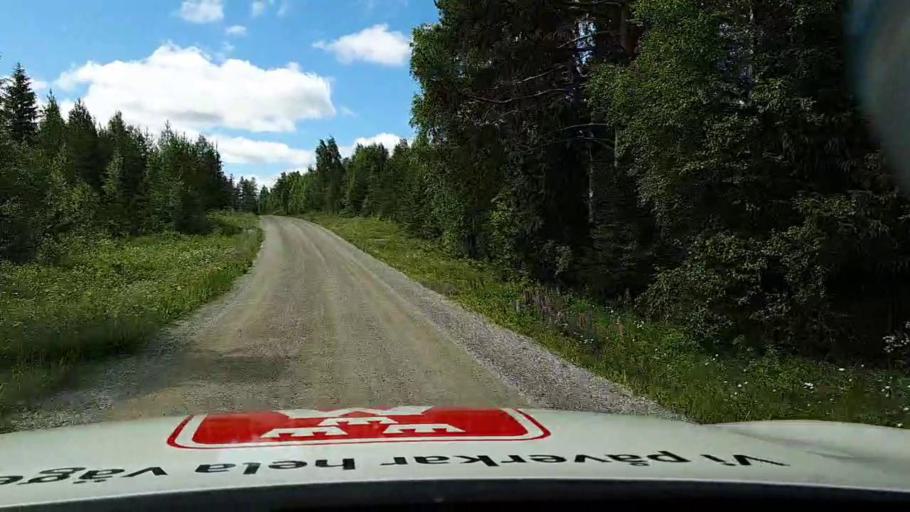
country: SE
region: Jaemtland
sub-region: Braecke Kommun
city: Braecke
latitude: 62.7416
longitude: 15.4964
